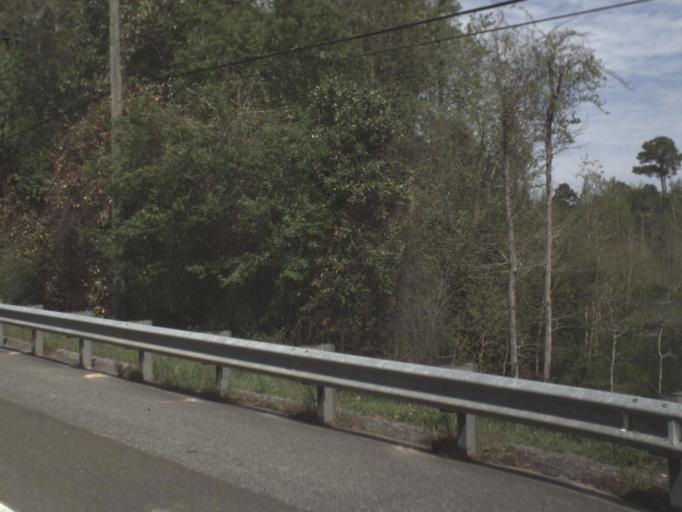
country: US
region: Florida
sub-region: Okaloosa County
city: Crestview
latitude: 30.7589
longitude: -86.5437
